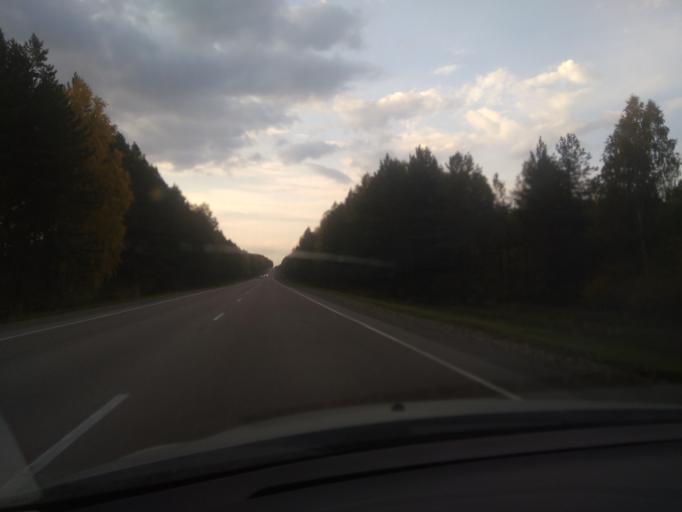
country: RU
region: Sverdlovsk
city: Dvurechensk
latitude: 56.6835
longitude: 61.1203
